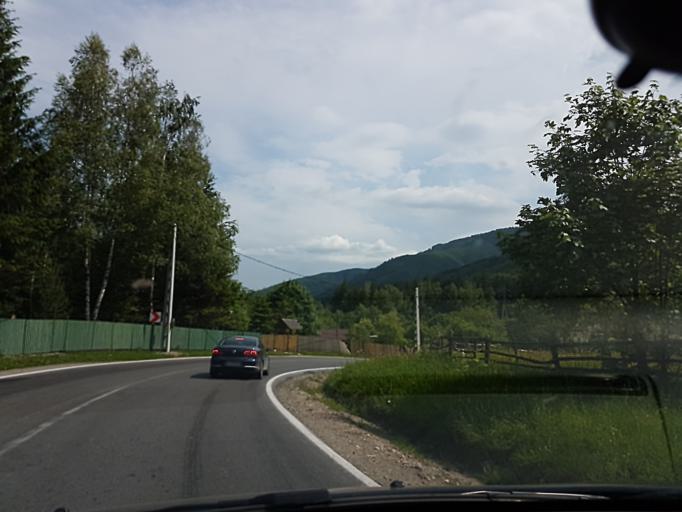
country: RO
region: Prahova
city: Maneciu
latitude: 45.3601
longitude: 25.9415
